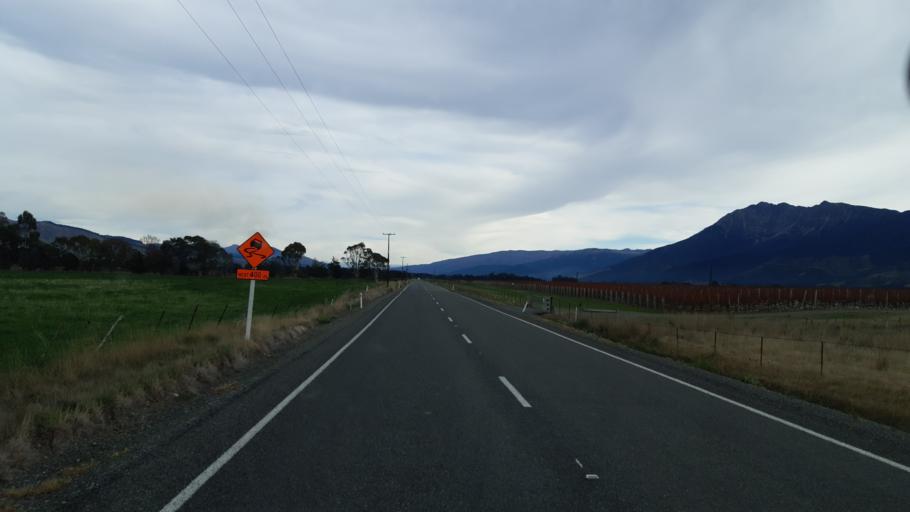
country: NZ
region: Tasman
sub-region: Tasman District
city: Richmond
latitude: -41.6201
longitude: 173.3665
